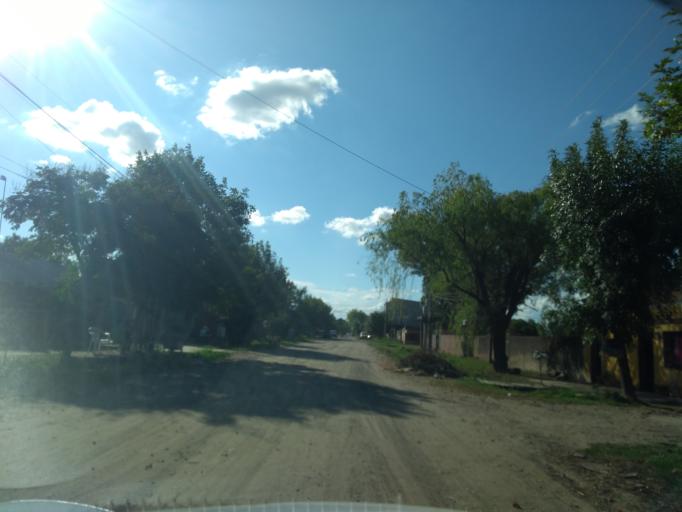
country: AR
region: Chaco
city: Resistencia
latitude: -27.4764
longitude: -58.9758
